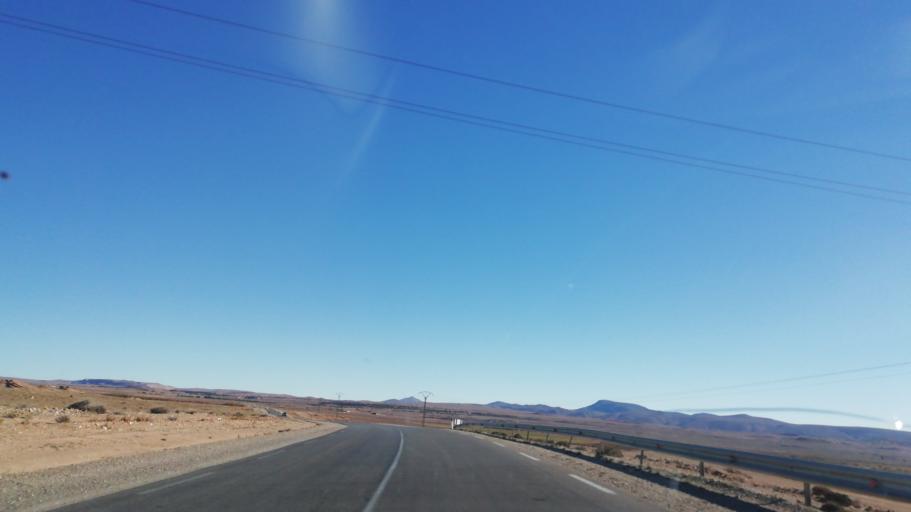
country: DZ
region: El Bayadh
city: El Bayadh
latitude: 33.6039
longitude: 1.2894
